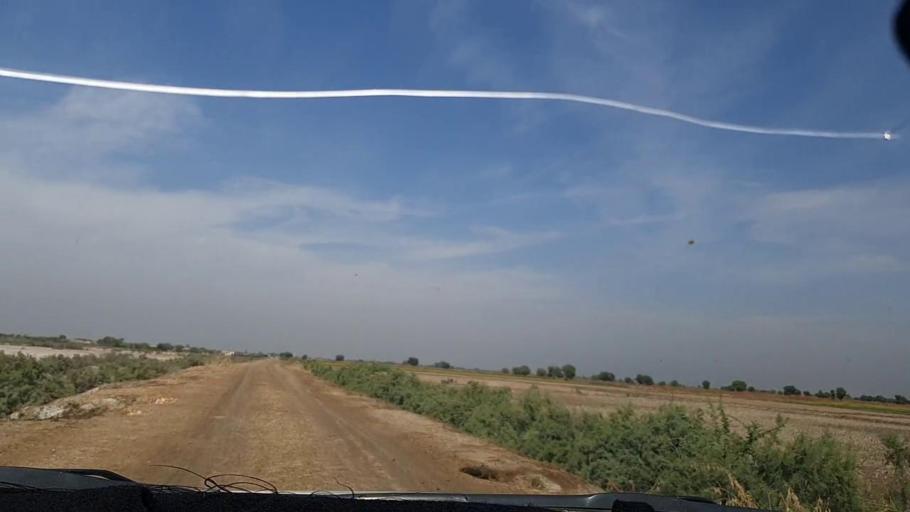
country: PK
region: Sindh
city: Pithoro
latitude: 25.4836
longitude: 69.4564
